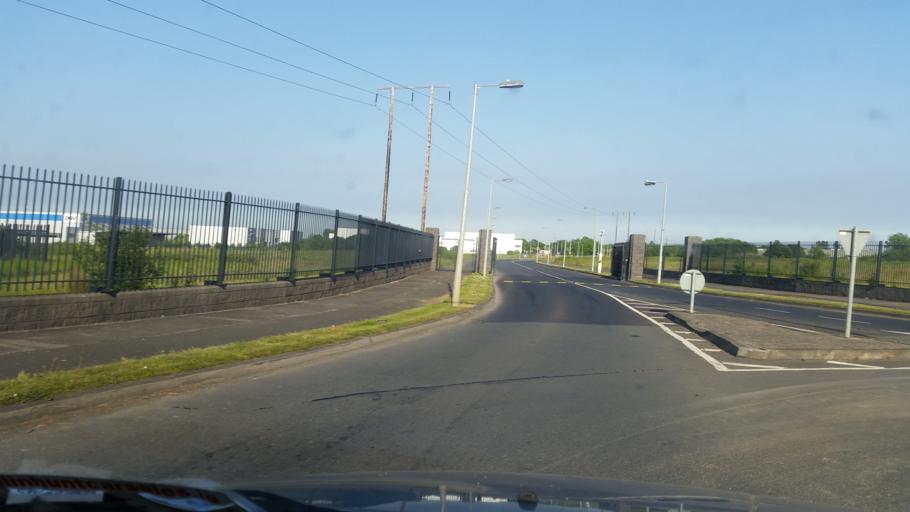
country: IE
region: Leinster
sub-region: Fingal County
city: Blanchardstown
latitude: 53.4178
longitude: -6.3569
